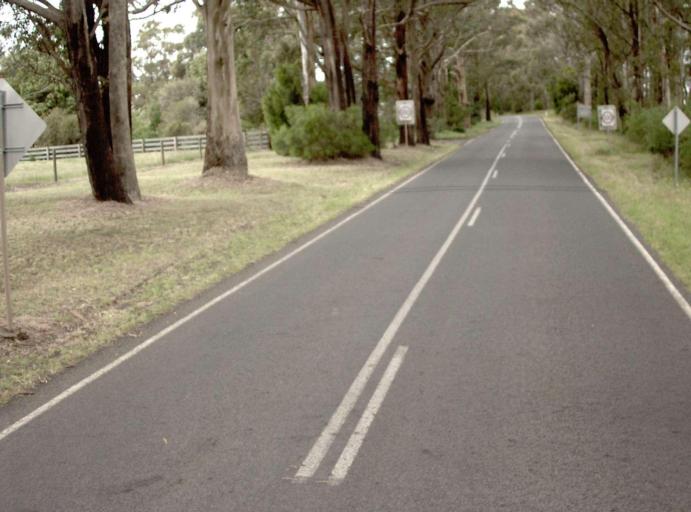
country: AU
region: Victoria
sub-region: Latrobe
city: Moe
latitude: -38.0141
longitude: 146.1500
